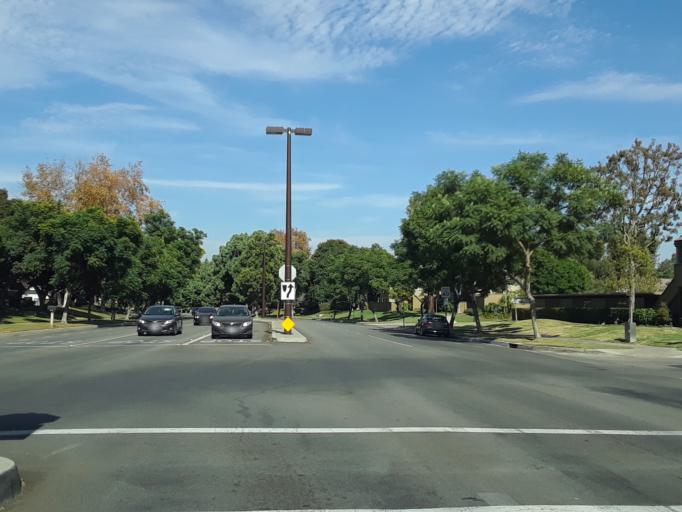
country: US
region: California
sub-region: Orange County
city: Irvine
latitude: 33.6762
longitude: -117.7864
